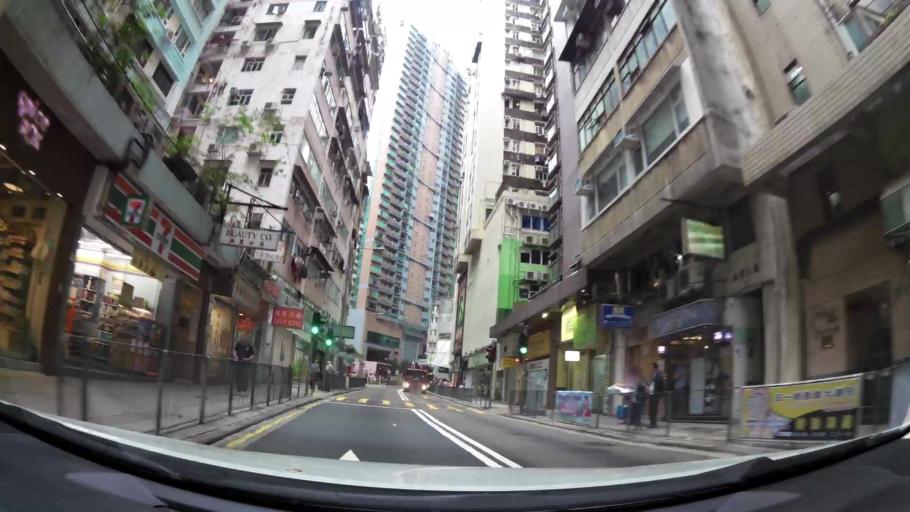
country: HK
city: Hong Kong
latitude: 22.2827
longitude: 114.1496
